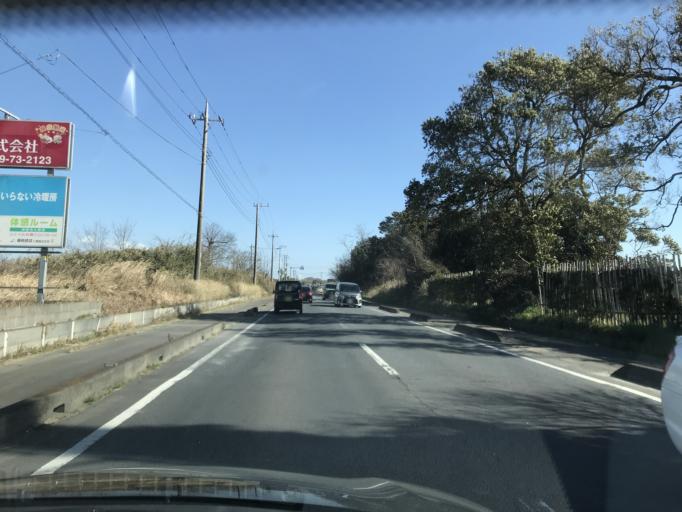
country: JP
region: Chiba
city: Omigawa
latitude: 35.8715
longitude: 140.6459
